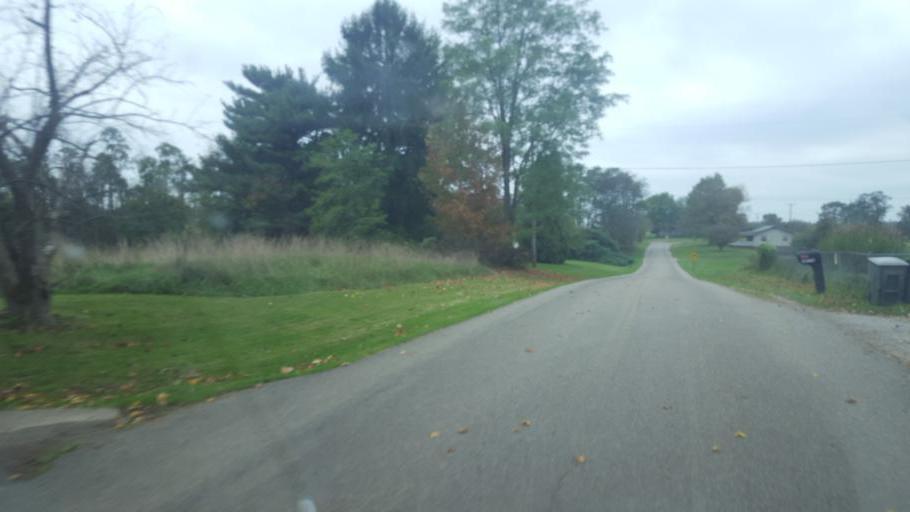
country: US
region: Ohio
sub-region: Harrison County
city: Cadiz
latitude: 40.3669
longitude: -81.0679
